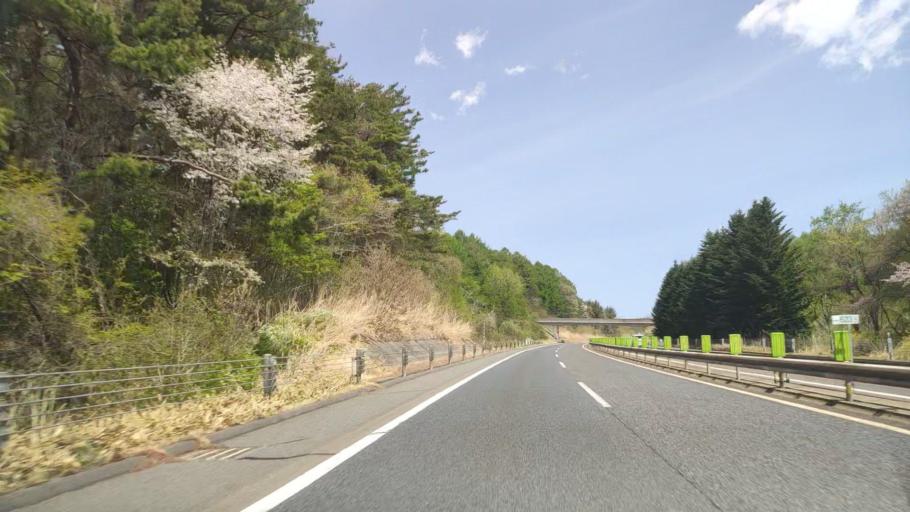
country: JP
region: Aomori
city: Hachinohe
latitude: 40.4273
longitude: 141.4399
